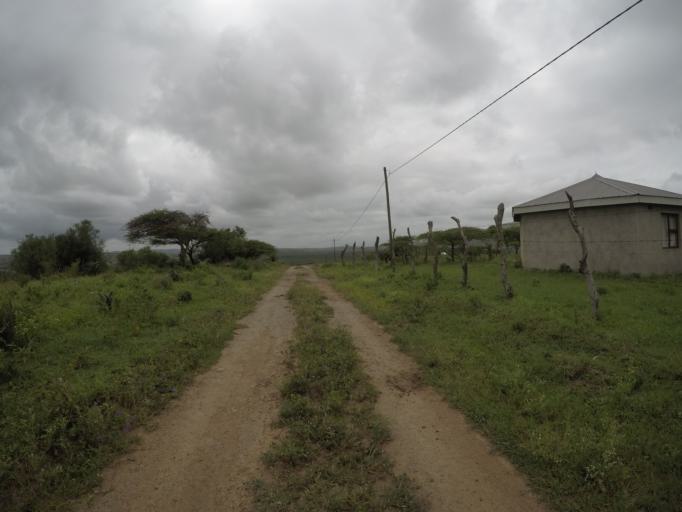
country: ZA
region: KwaZulu-Natal
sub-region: uThungulu District Municipality
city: Empangeni
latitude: -28.5964
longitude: 31.8505
